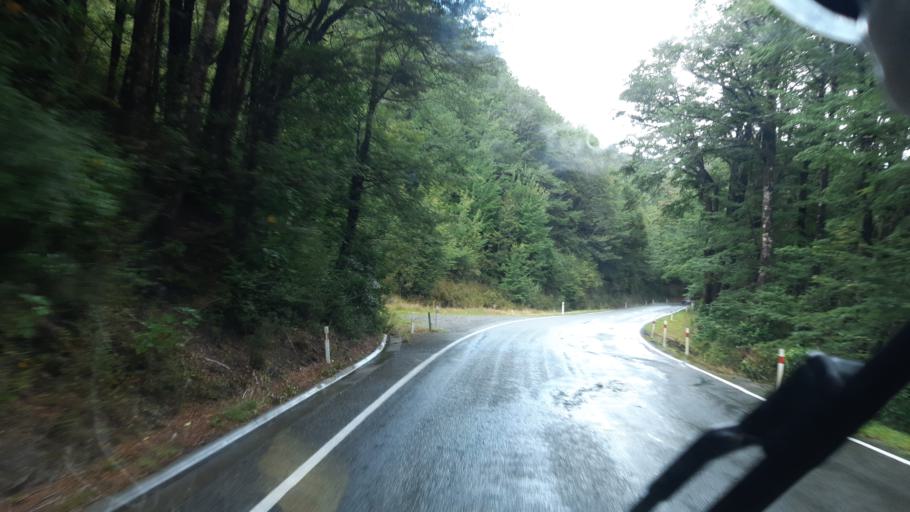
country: NZ
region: Canterbury
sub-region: Hurunui District
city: Amberley
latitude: -42.3754
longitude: 172.3630
